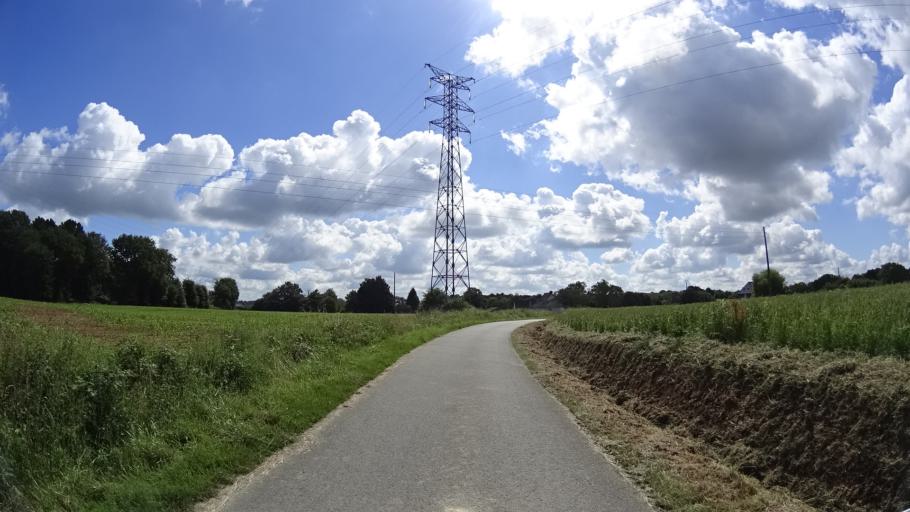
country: FR
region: Brittany
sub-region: Departement d'Ille-et-Vilaine
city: Le Rheu
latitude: 48.1161
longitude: -1.8041
